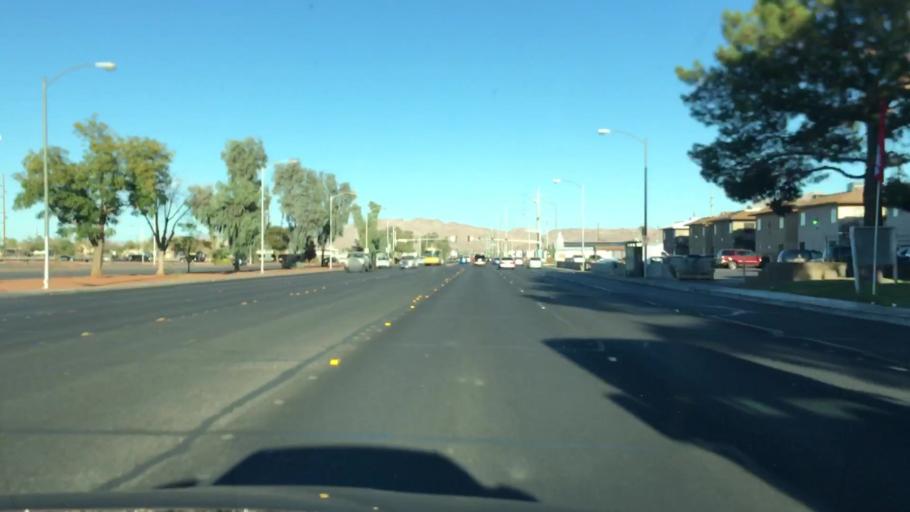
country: US
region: Nevada
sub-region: Clark County
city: North Las Vegas
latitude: 36.2176
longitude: -115.1012
